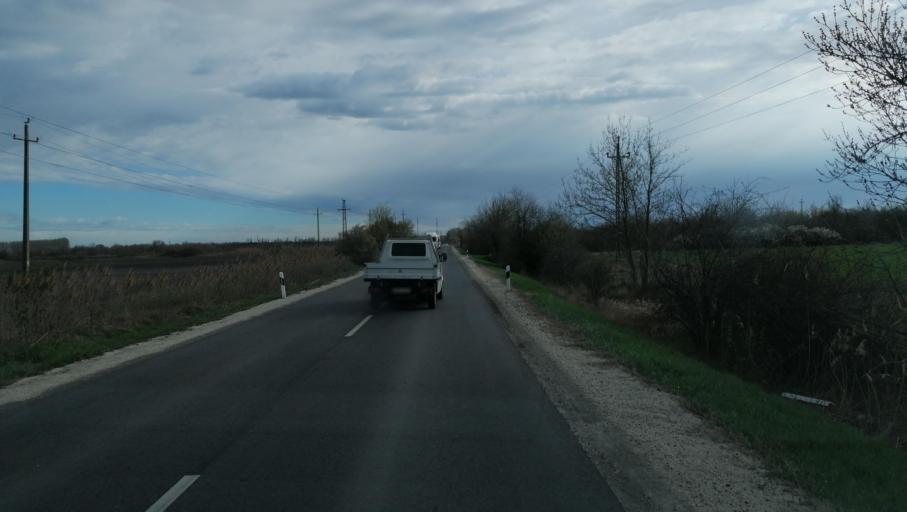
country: HU
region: Pest
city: Ocsa
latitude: 47.2504
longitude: 19.2067
